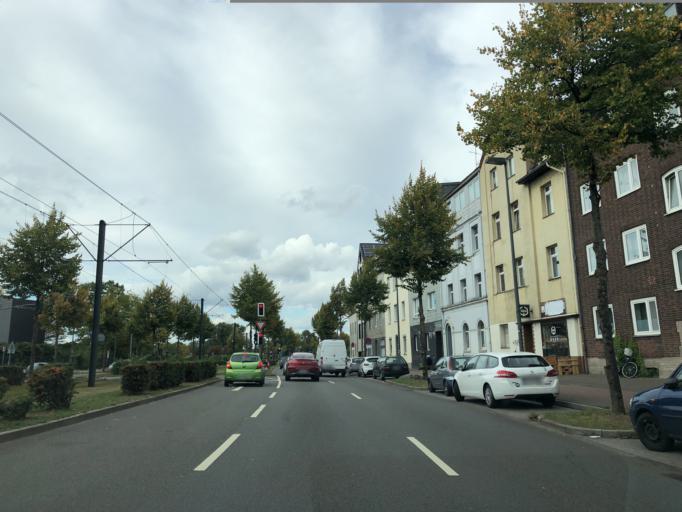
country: DE
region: North Rhine-Westphalia
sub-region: Regierungsbezirk Dusseldorf
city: Dusseldorf
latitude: 51.1999
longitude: 6.8118
